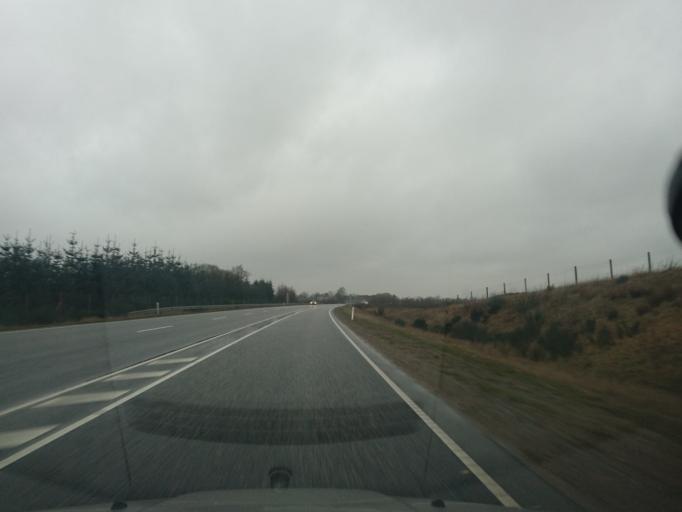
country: DK
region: South Denmark
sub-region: Vejle Kommune
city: Egtved
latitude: 55.7081
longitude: 9.2374
